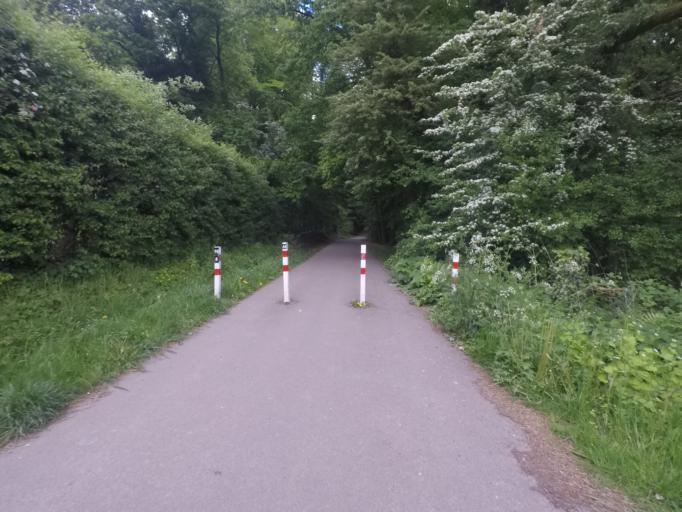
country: DE
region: North Rhine-Westphalia
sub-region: Regierungsbezirk Detmold
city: Bad Salzuflen
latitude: 52.1125
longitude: 8.7163
